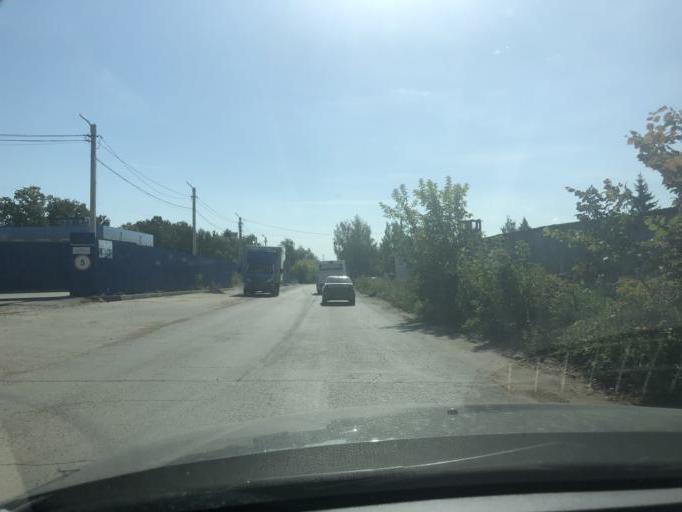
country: RU
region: Tula
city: Skuratovskiy
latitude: 54.1278
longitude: 37.6256
